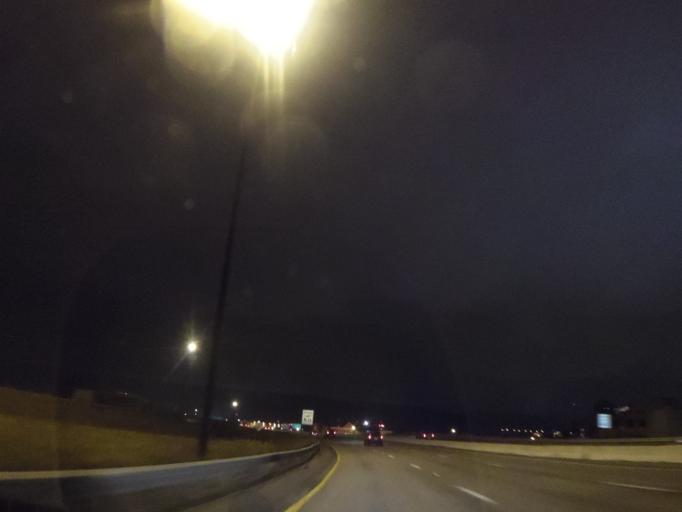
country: US
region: Indiana
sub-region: Marion County
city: Indianapolis
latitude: 39.7764
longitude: -86.1422
